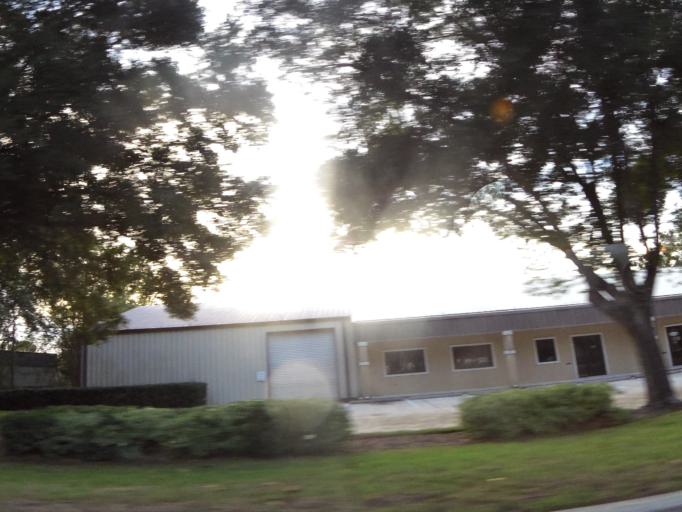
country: US
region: Florida
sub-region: Saint Johns County
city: Fruit Cove
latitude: 30.1562
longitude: -81.5366
